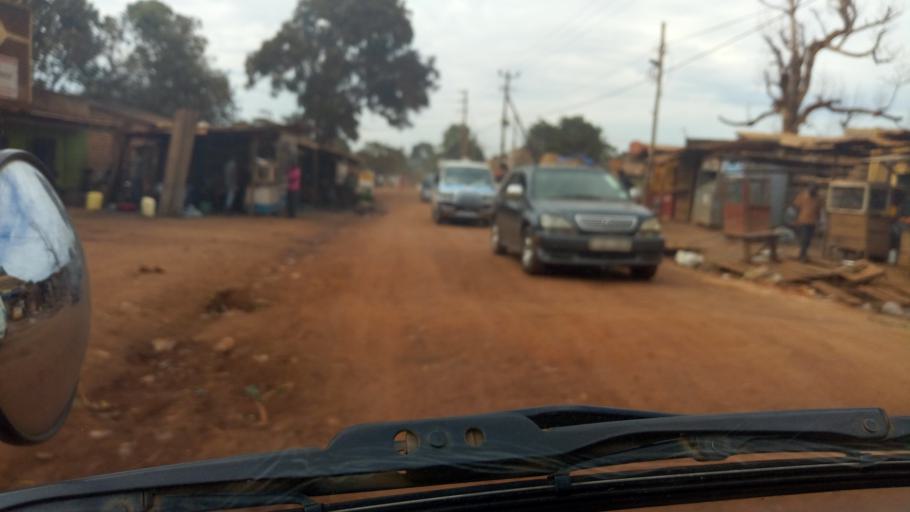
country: UG
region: Central Region
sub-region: Wakiso District
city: Bweyogerere
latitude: 0.3613
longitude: 32.7035
